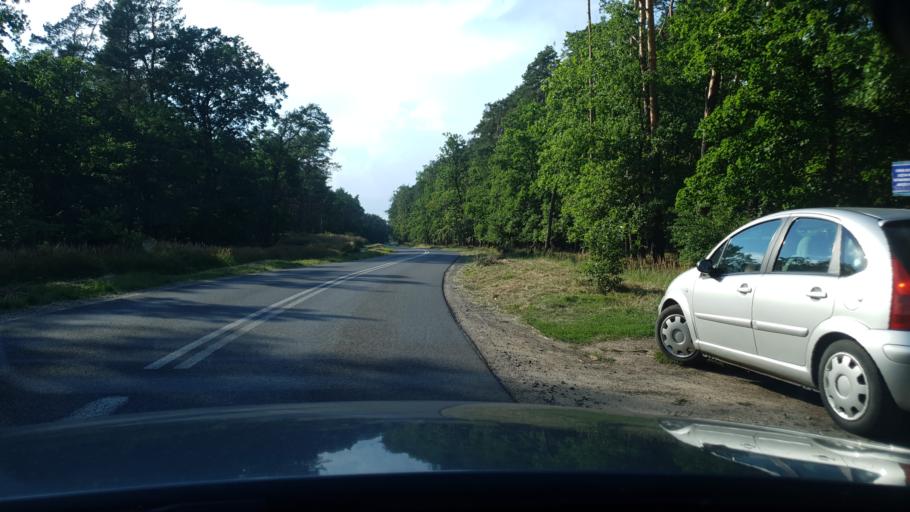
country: PL
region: Kujawsko-Pomorskie
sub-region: Grudziadz
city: Grudziadz
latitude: 53.4458
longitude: 18.7442
